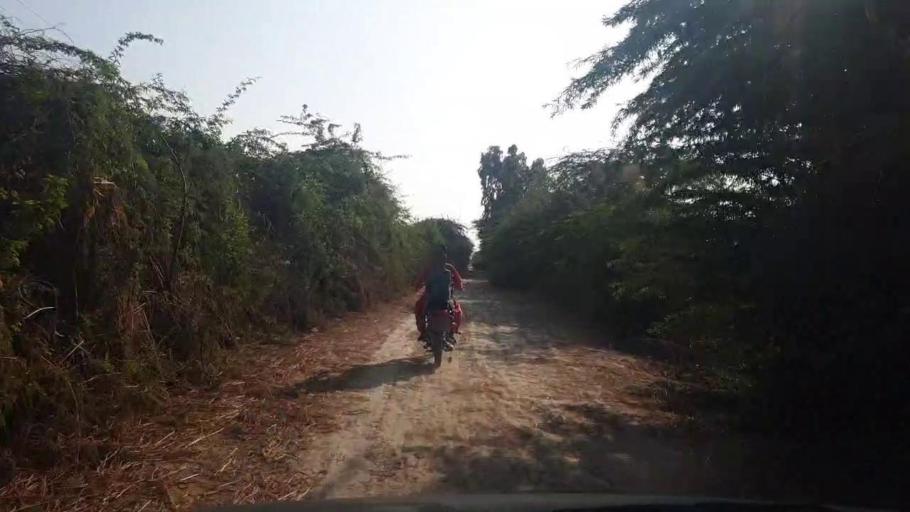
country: PK
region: Sindh
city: Badin
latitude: 24.6448
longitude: 68.8039
